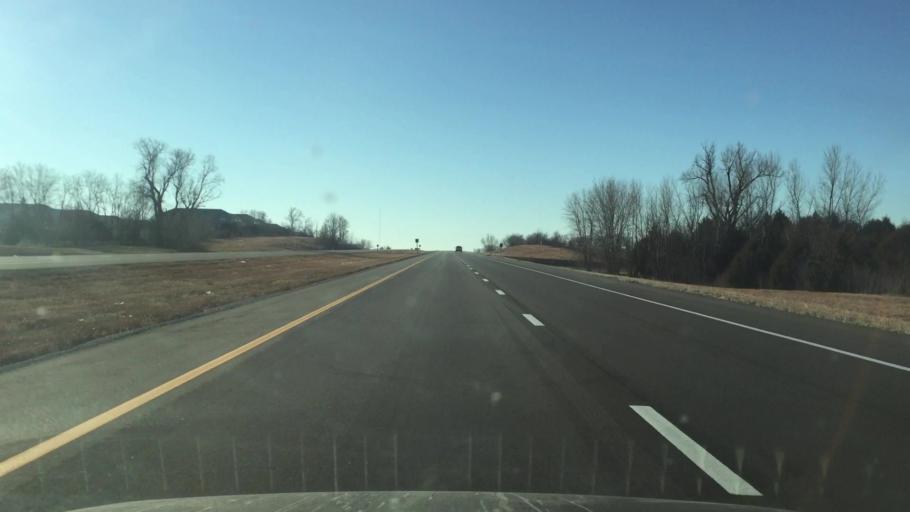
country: US
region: Kansas
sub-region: Johnson County
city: Spring Hill
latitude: 38.7475
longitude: -94.8394
